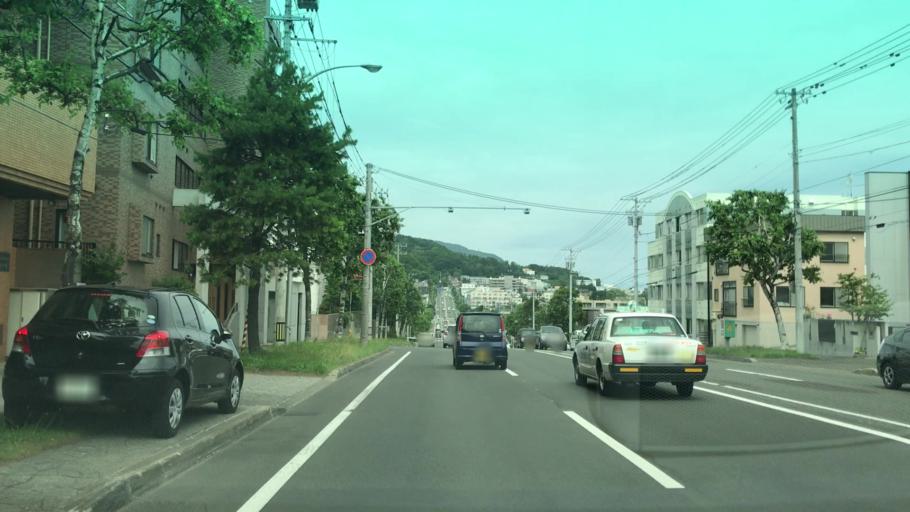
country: JP
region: Hokkaido
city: Sapporo
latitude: 43.0594
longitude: 141.2989
